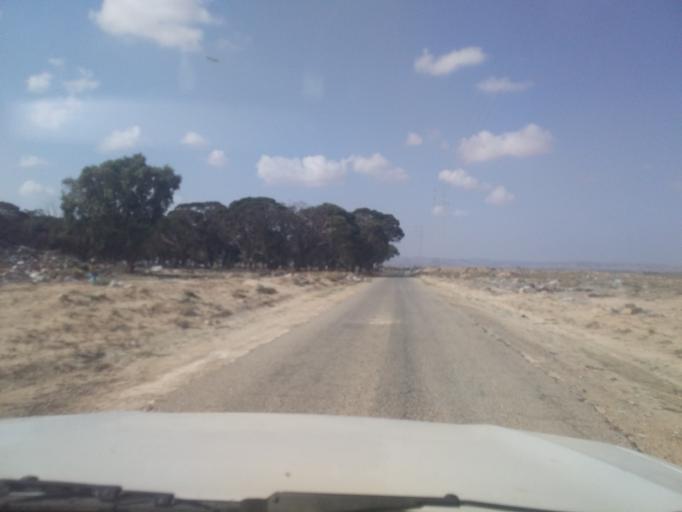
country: TN
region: Qabis
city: Gabes
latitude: 33.6295
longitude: 10.2717
